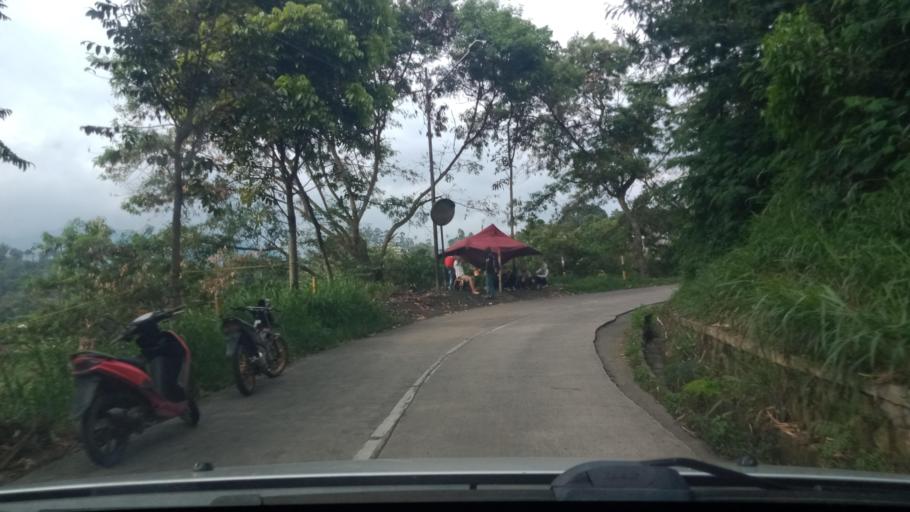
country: ID
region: West Java
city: Lembang
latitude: -6.8230
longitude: 107.5742
